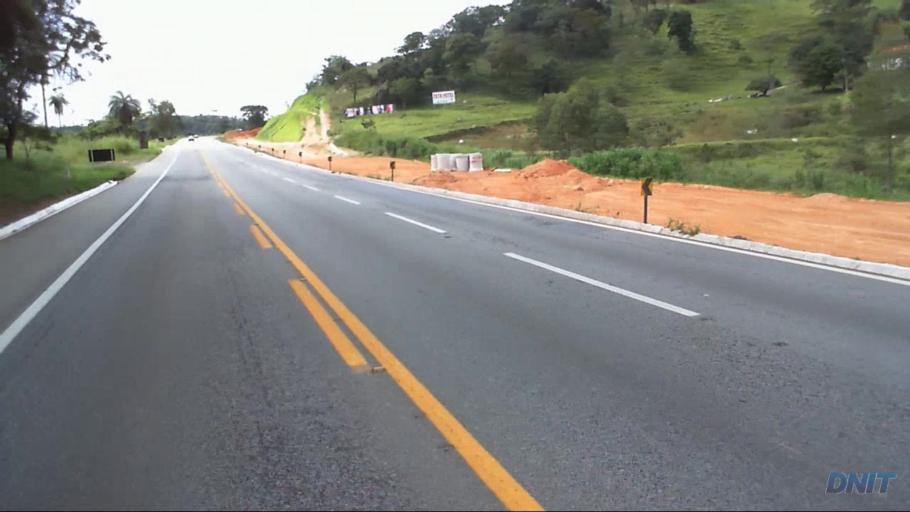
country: BR
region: Minas Gerais
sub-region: Caete
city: Caete
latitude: -19.7442
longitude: -43.6158
